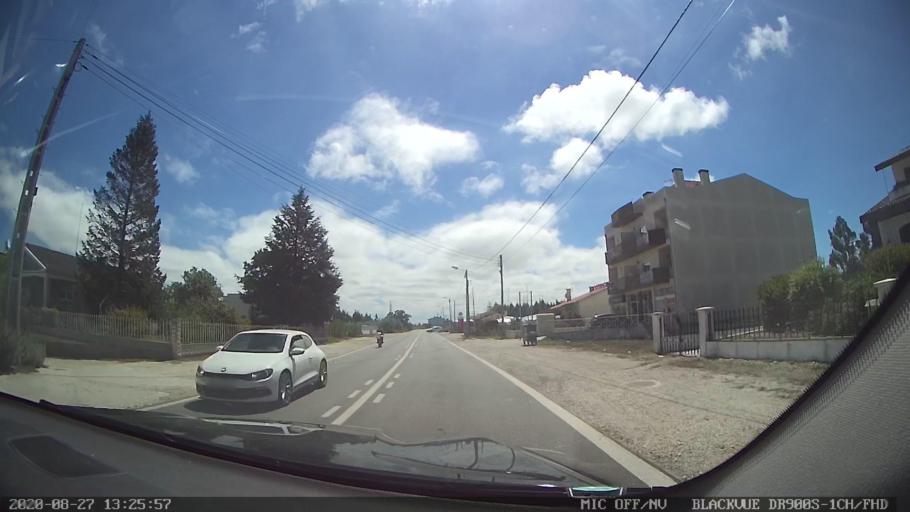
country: PT
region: Aveiro
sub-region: Vagos
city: Vagos
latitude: 40.5418
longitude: -8.6778
